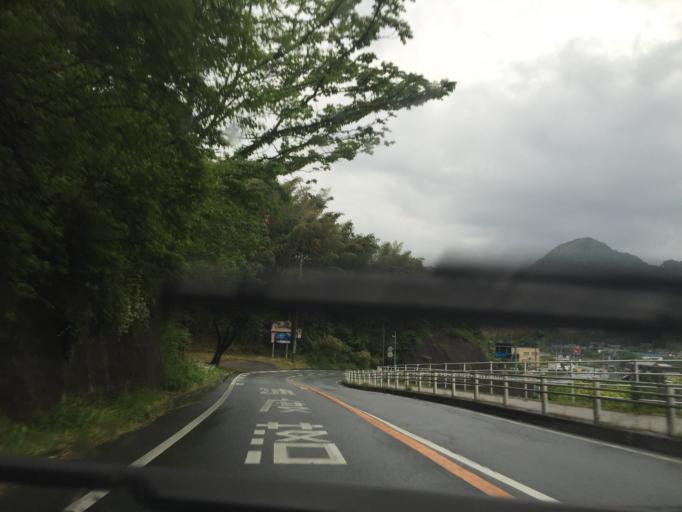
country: JP
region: Shizuoka
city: Mishima
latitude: 35.0433
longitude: 138.9205
